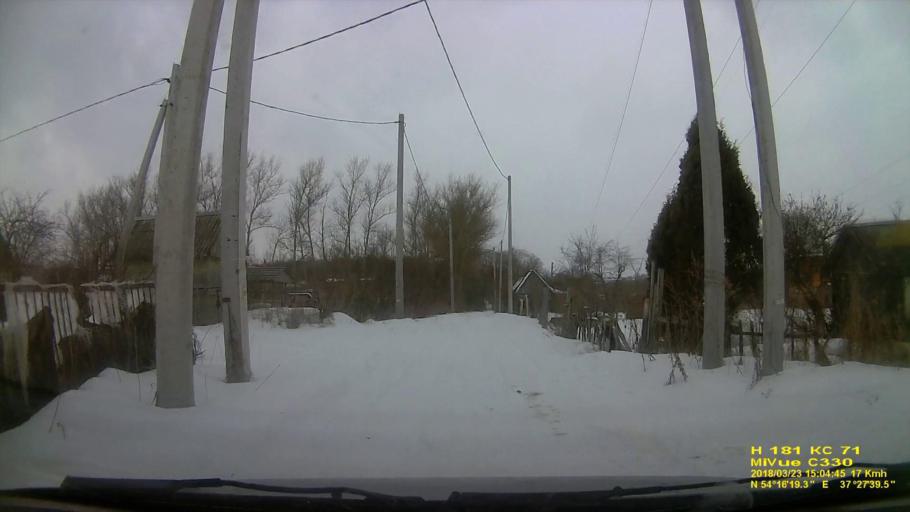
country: RU
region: Tula
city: Leninskiy
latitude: 54.2721
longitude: 37.4609
